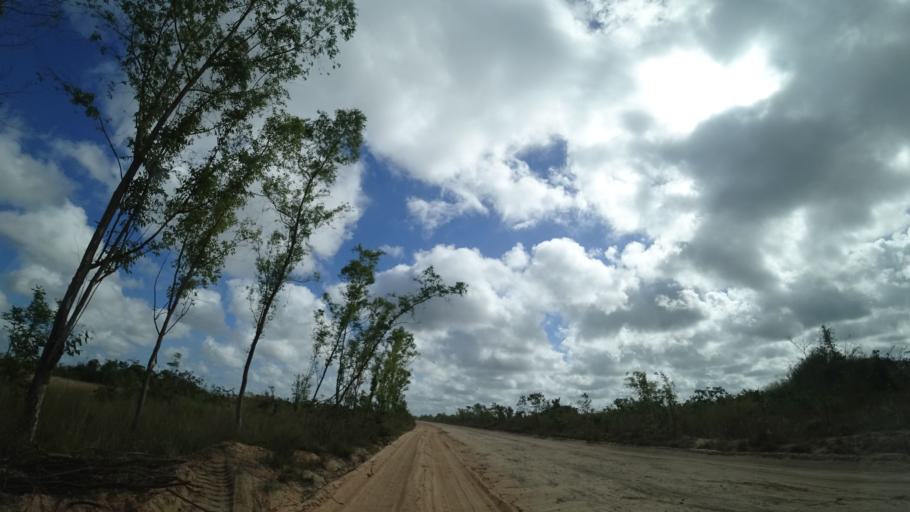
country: MZ
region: Sofala
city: Dondo
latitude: -19.4545
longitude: 34.7185
